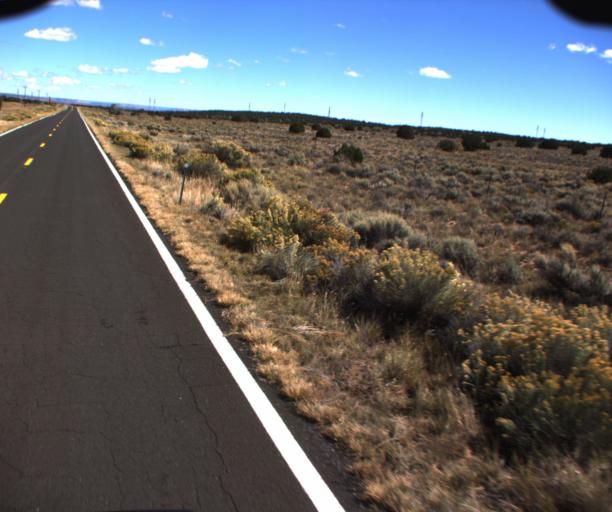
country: US
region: New Mexico
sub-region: McKinley County
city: Zuni Pueblo
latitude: 35.0127
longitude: -109.0637
